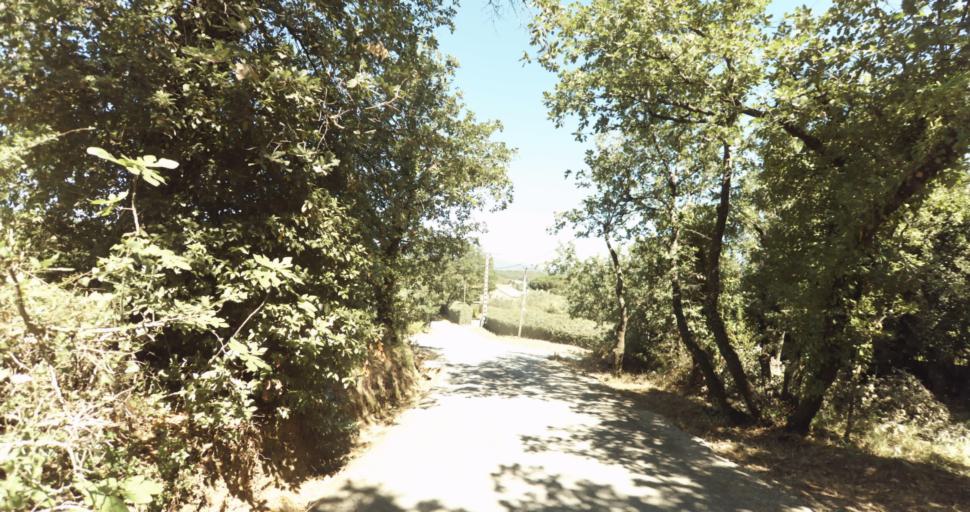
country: FR
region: Provence-Alpes-Cote d'Azur
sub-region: Departement du Var
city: Gassin
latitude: 43.2354
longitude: 6.5779
